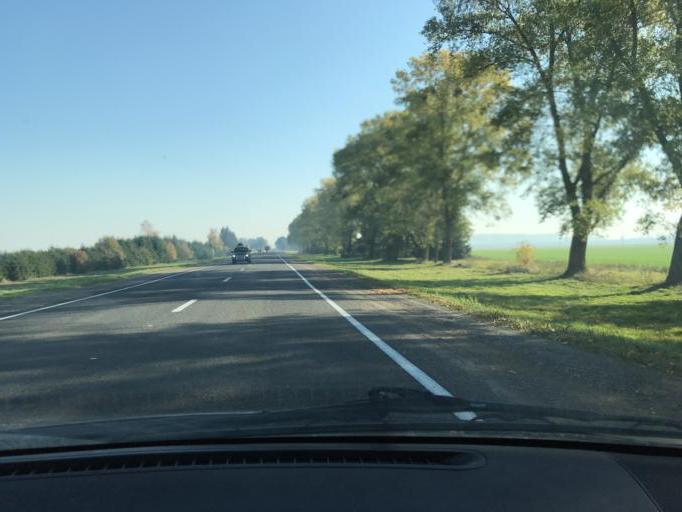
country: BY
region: Minsk
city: Klyetsk
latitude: 52.9713
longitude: 26.6762
